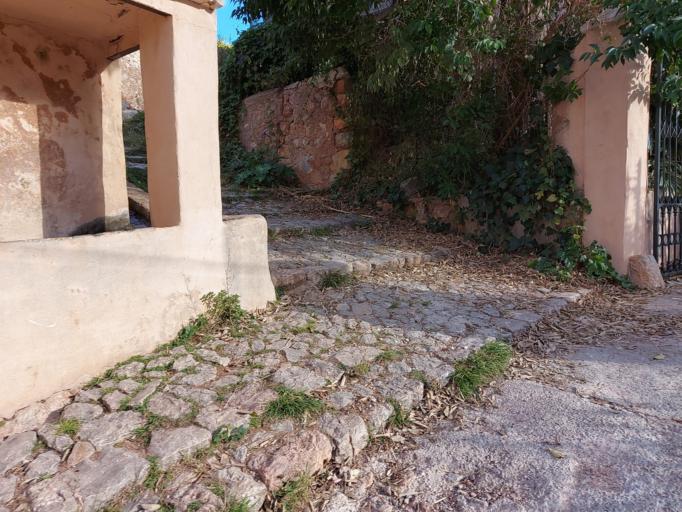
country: ES
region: Balearic Islands
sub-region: Illes Balears
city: Fornalutx
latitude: 39.7772
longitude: 2.7285
